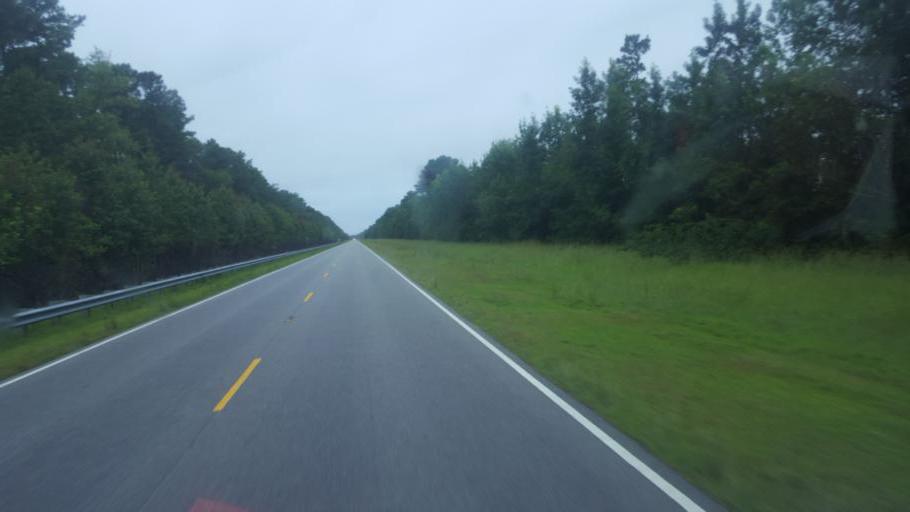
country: US
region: North Carolina
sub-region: Tyrrell County
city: Columbia
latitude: 35.9144
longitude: -76.1185
